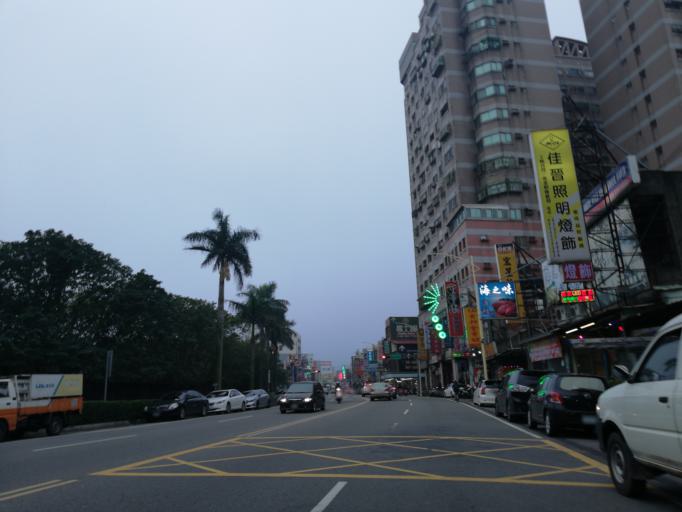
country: TW
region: Taiwan
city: Taoyuan City
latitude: 24.9716
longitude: 121.3017
